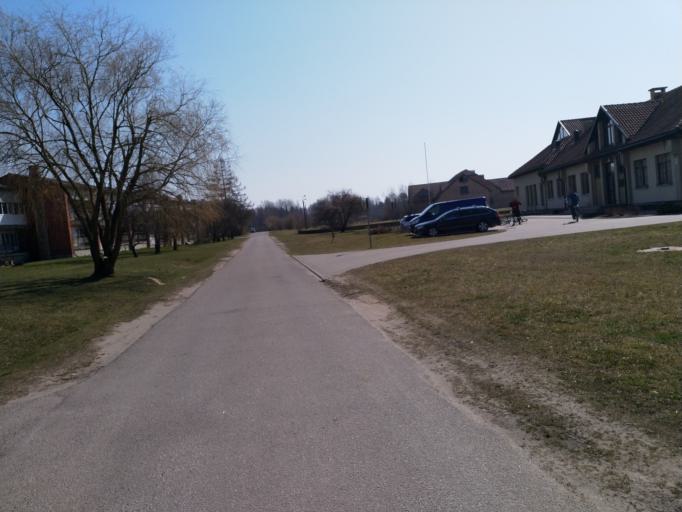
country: LV
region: Aizpute
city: Aizpute
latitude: 56.7131
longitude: 21.5640
